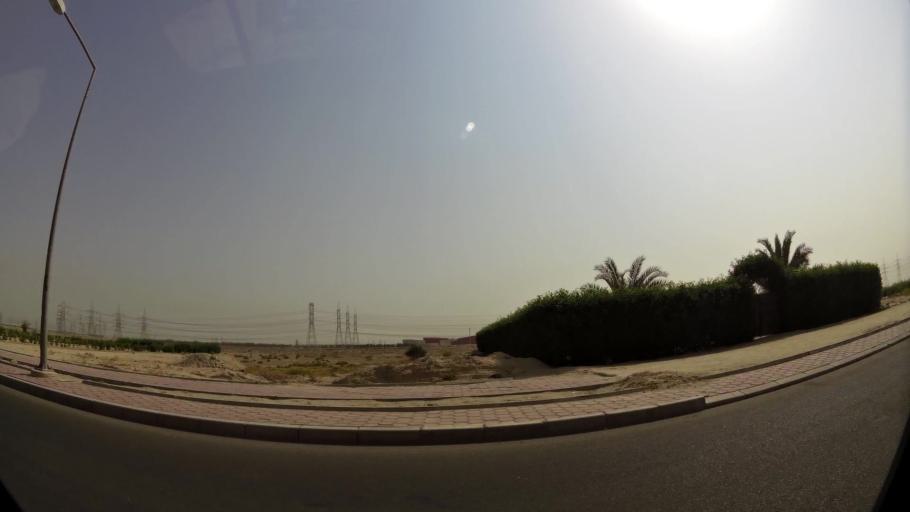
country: KW
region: Muhafazat al Jahra'
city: Al Jahra'
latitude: 29.3261
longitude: 47.7792
